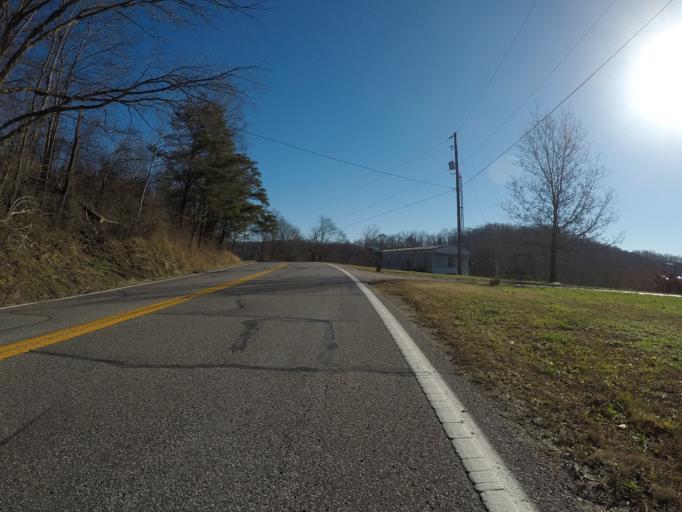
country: US
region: West Virginia
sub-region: Cabell County
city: Huntington
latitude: 38.4838
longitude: -82.4591
